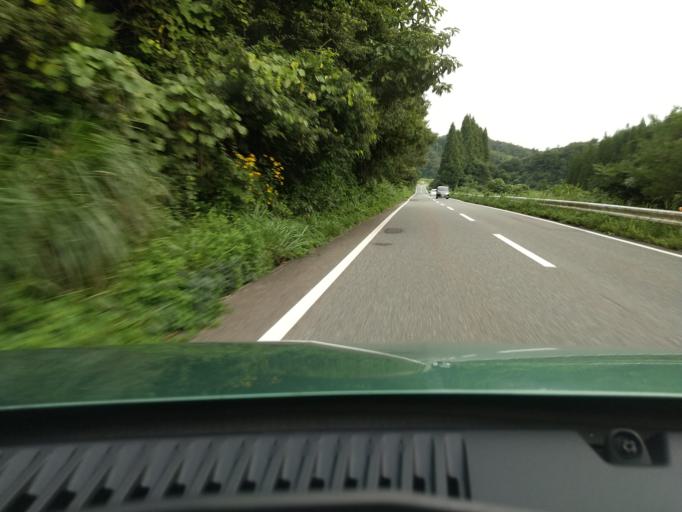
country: JP
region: Akita
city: Akita
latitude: 39.7515
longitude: 140.1596
